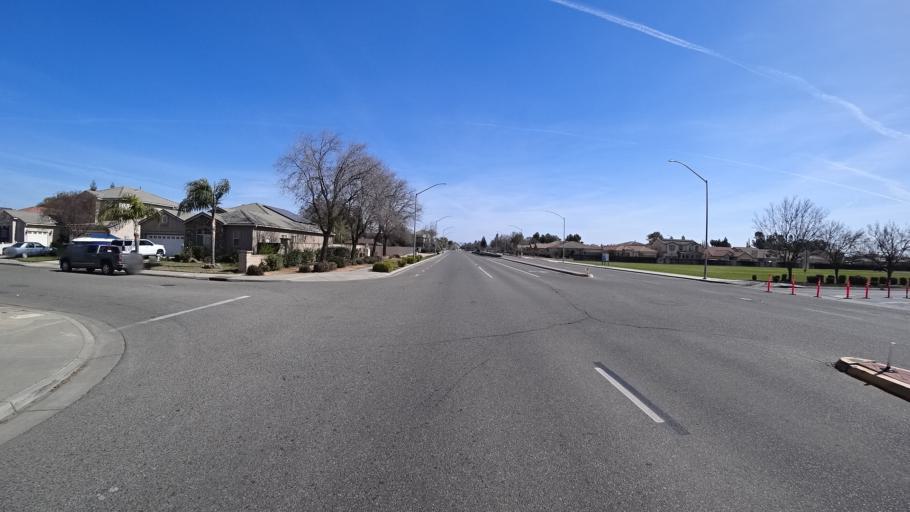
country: US
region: California
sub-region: Fresno County
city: Clovis
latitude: 36.8522
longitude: -119.7338
